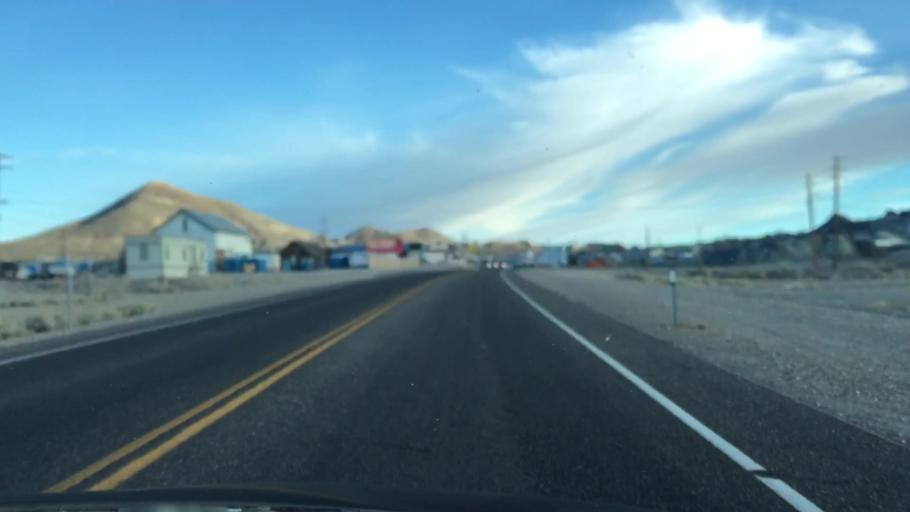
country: US
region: Nevada
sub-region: Nye County
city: Tonopah
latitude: 38.0759
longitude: -117.2442
